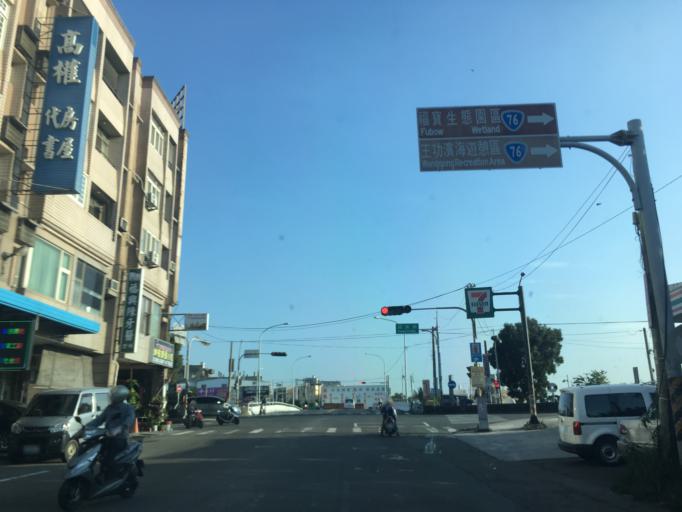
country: TW
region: Taiwan
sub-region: Changhua
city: Chang-hua
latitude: 24.0468
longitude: 120.4367
